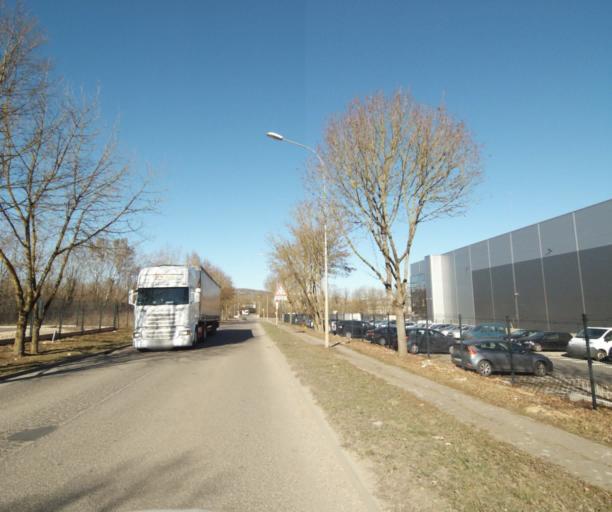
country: FR
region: Lorraine
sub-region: Departement de Meurthe-et-Moselle
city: Fleville-devant-Nancy
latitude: 48.6090
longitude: 6.1929
